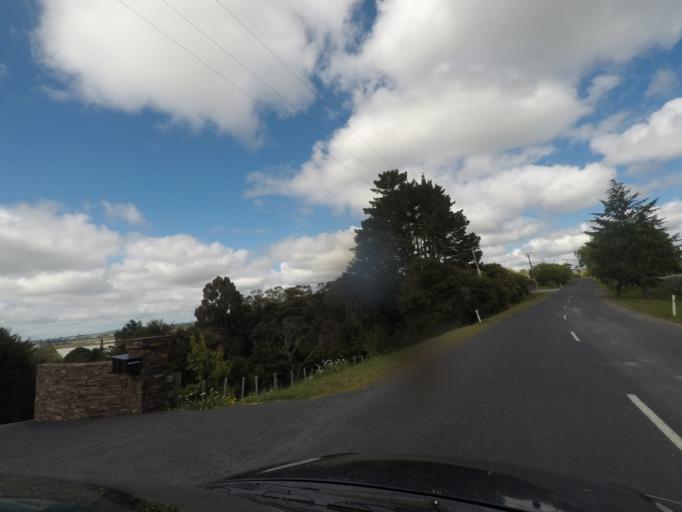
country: NZ
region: Auckland
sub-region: Auckland
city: Rothesay Bay
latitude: -36.7639
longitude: 174.6466
